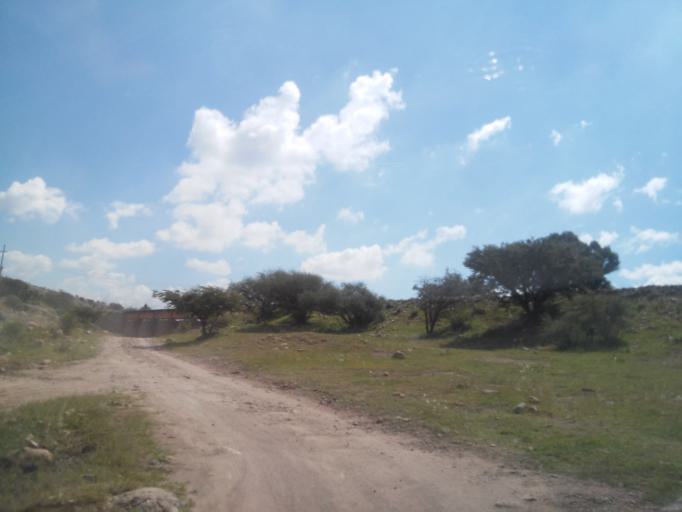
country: MX
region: Durango
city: Victoria de Durango
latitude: 24.0131
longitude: -104.7431
